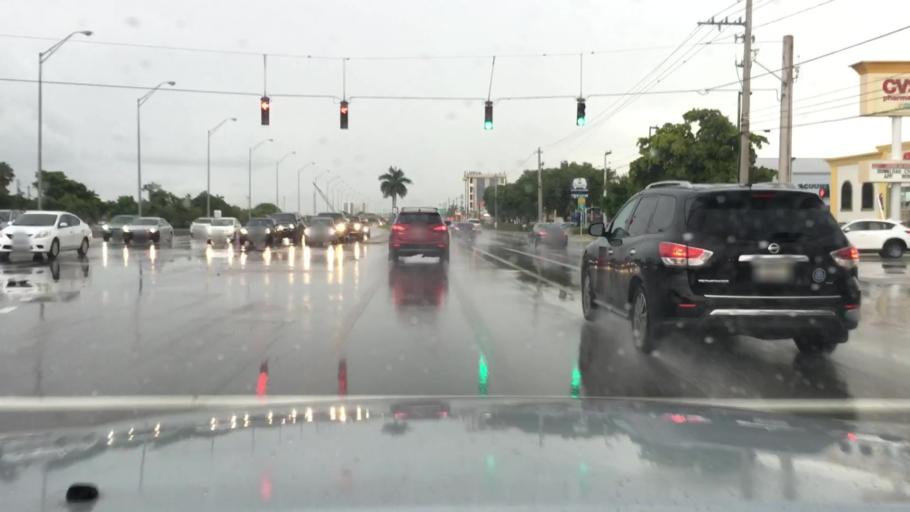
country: US
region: Florida
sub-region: Miami-Dade County
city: Tamiami
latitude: 25.7602
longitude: -80.3953
